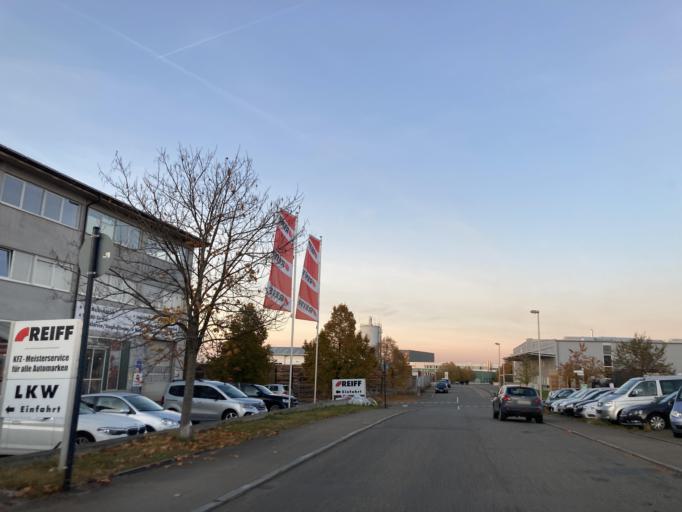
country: DE
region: Baden-Wuerttemberg
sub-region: Tuebingen Region
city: Mossingen
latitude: 48.4136
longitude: 9.0512
